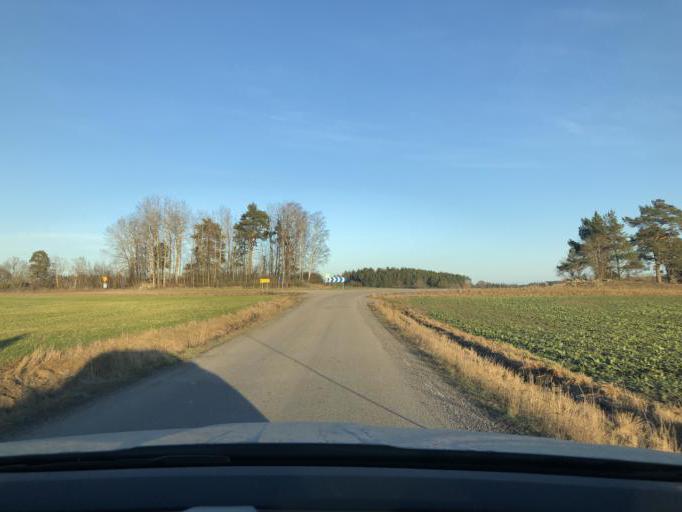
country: SE
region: Soedermanland
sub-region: Eskilstuna Kommun
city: Arla
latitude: 59.4182
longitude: 16.6749
